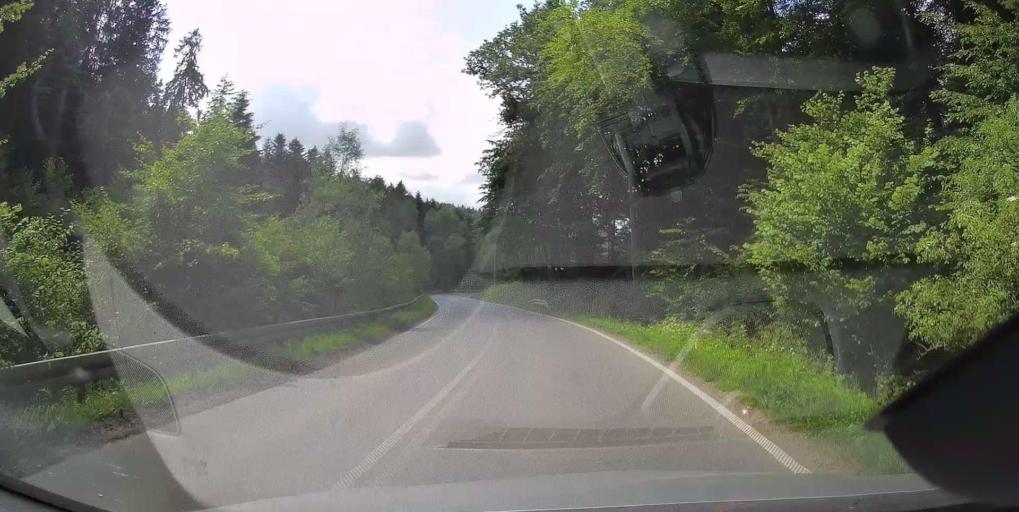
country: PL
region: Lesser Poland Voivodeship
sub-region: Powiat nowosadecki
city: Nowy Sacz
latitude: 49.6642
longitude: 20.7346
